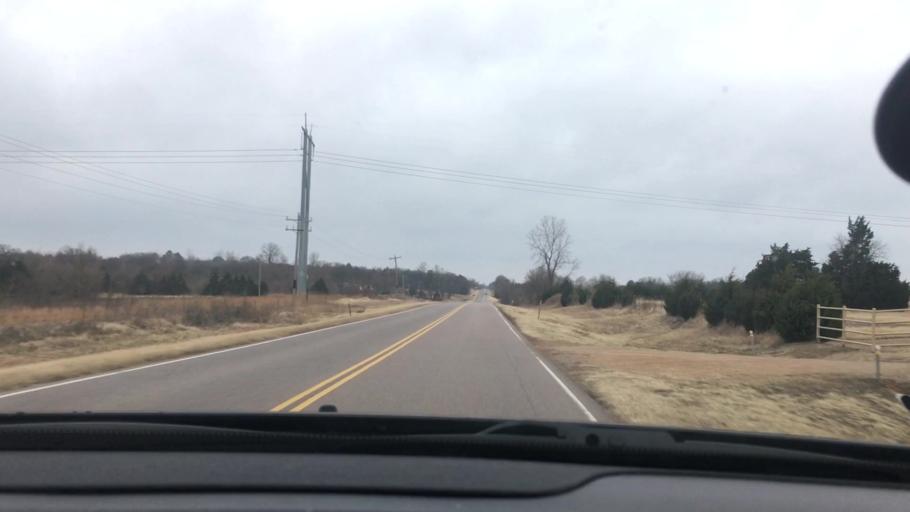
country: US
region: Oklahoma
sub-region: Johnston County
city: Tishomingo
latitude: 34.2682
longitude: -96.6711
